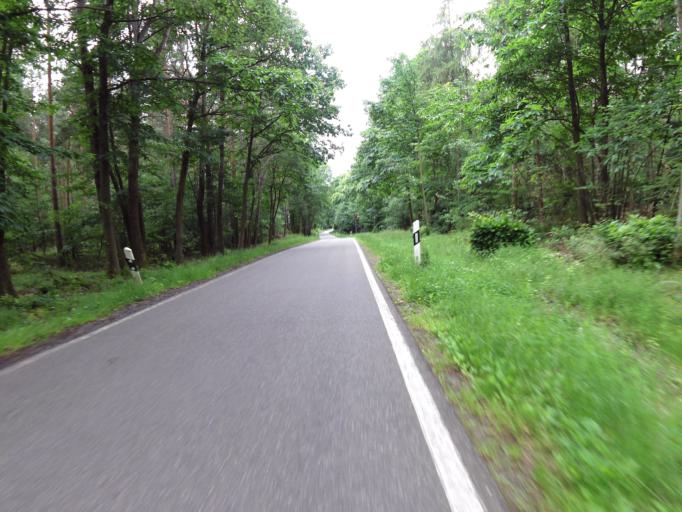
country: DE
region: Rheinland-Pfalz
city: Kallstadt
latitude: 49.4798
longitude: 8.1489
